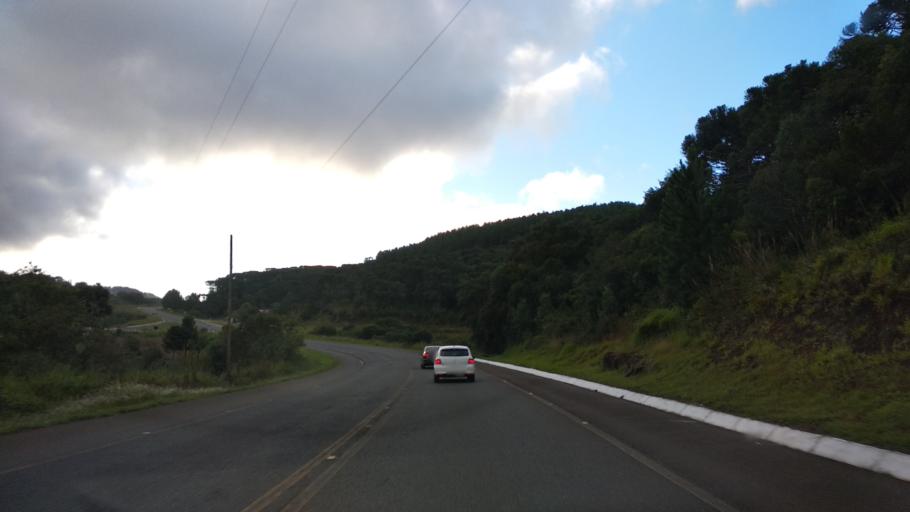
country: BR
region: Santa Catarina
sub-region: Curitibanos
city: Curitibanos
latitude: -27.5787
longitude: -50.7743
